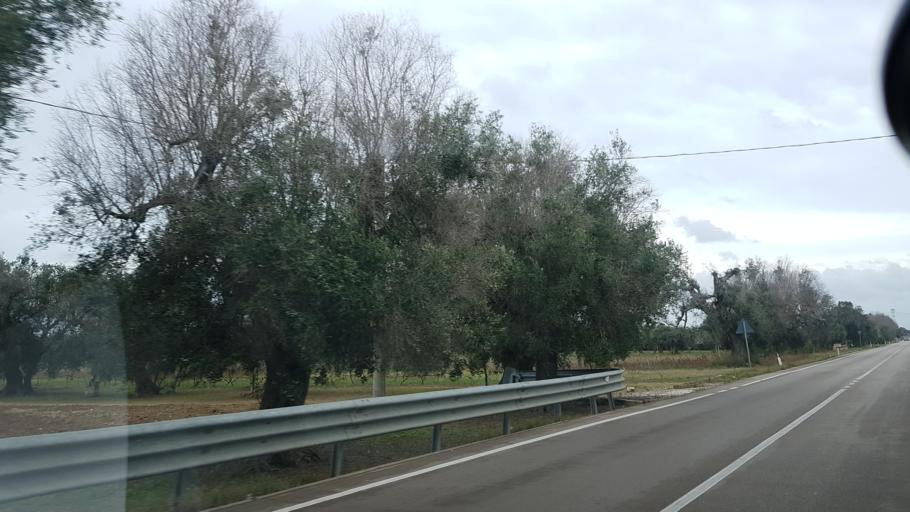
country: IT
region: Apulia
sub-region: Provincia di Lecce
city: Guagnano
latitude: 40.4008
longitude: 17.9638
